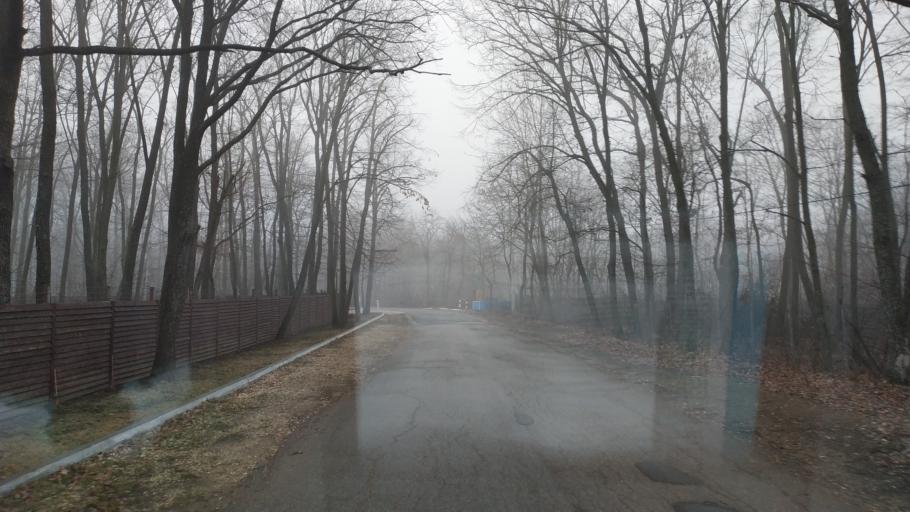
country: MD
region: Laloveni
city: Ialoveni
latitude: 46.9456
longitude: 28.7031
